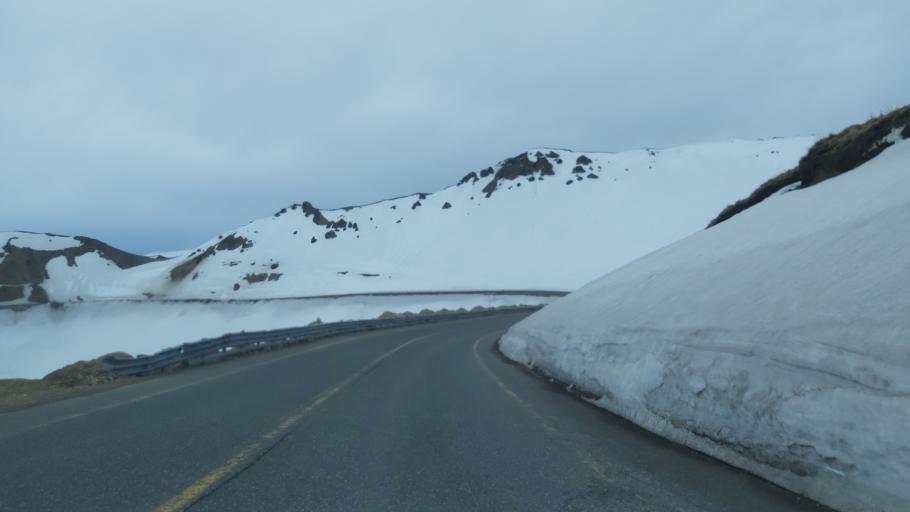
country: CL
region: Maule
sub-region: Provincia de Linares
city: Colbun
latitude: -36.0178
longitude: -70.5050
